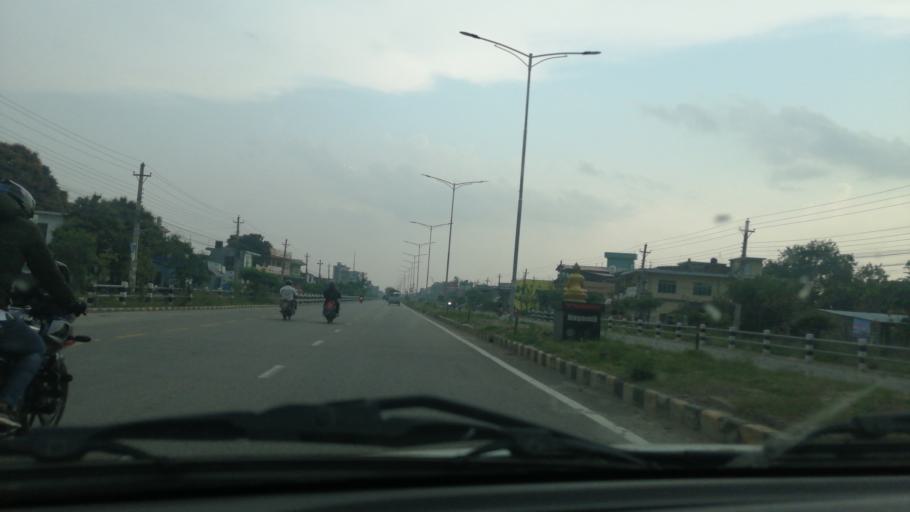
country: NP
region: Western Region
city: Butwal
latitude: 27.6359
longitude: 83.4719
